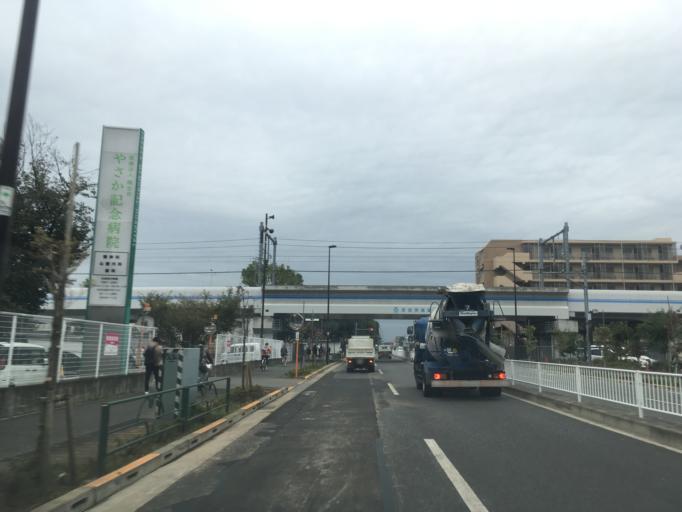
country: JP
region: Tokyo
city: Higashimurayama-shi
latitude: 35.7427
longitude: 139.4668
